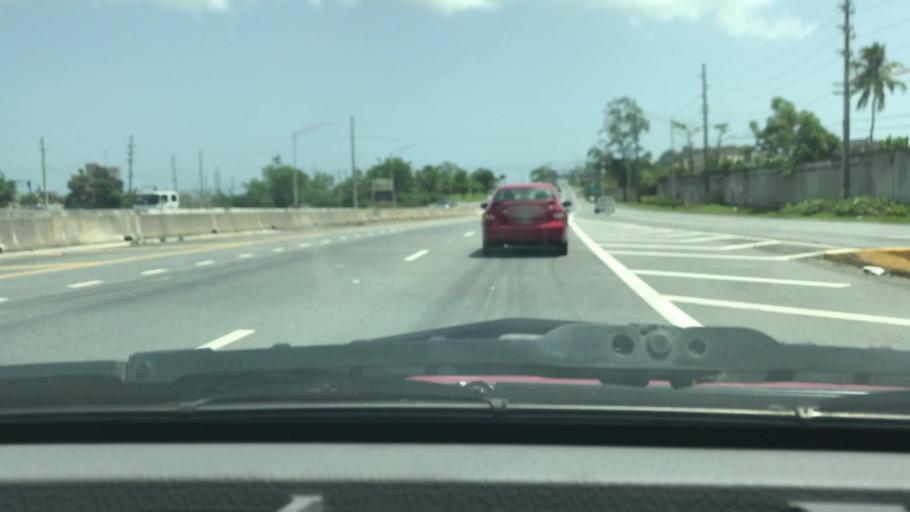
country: PR
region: Bayamon
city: Bayamon
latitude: 18.3889
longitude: -66.1543
